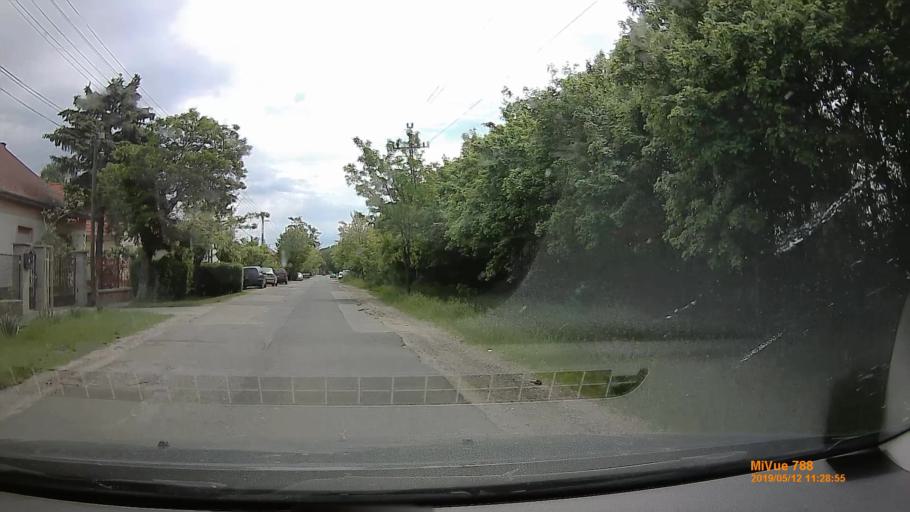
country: HU
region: Budapest
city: Budapest XVII. keruelet
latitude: 47.4653
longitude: 19.2492
